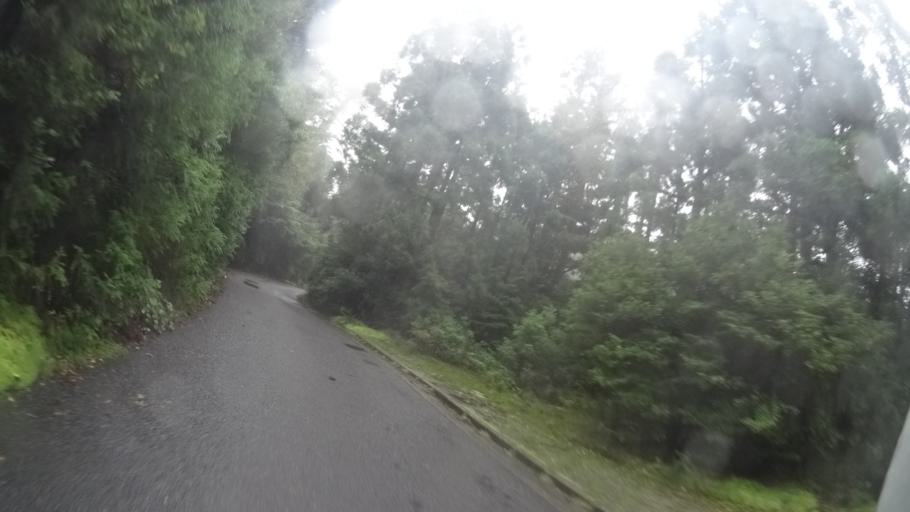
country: JP
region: Kagoshima
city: Nishinoomote
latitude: 30.3026
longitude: 130.5793
